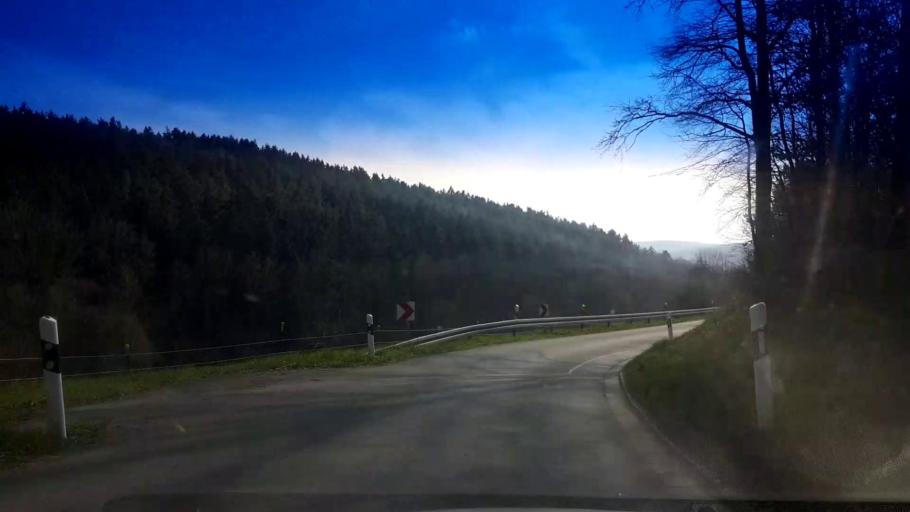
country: DE
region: Bavaria
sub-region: Upper Franconia
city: Harsdorf
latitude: 50.0327
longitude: 11.5807
